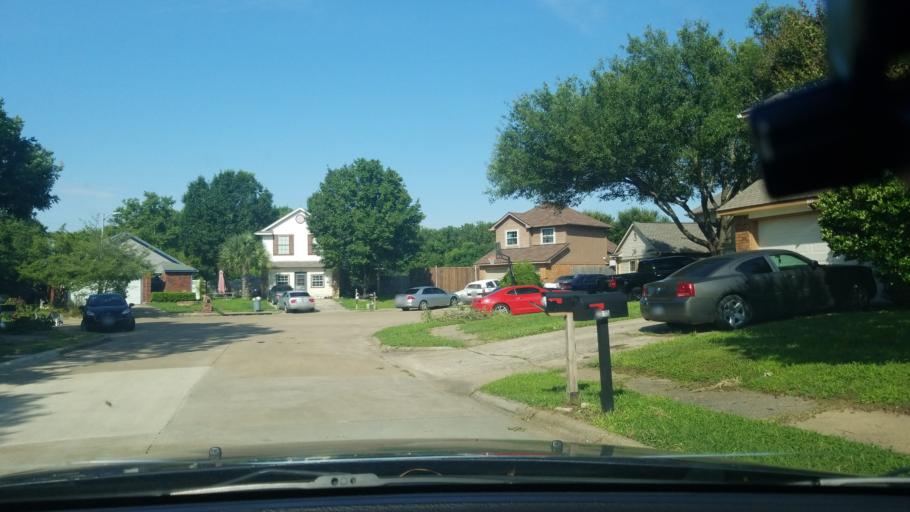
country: US
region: Texas
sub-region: Dallas County
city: Mesquite
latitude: 32.7770
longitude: -96.5792
